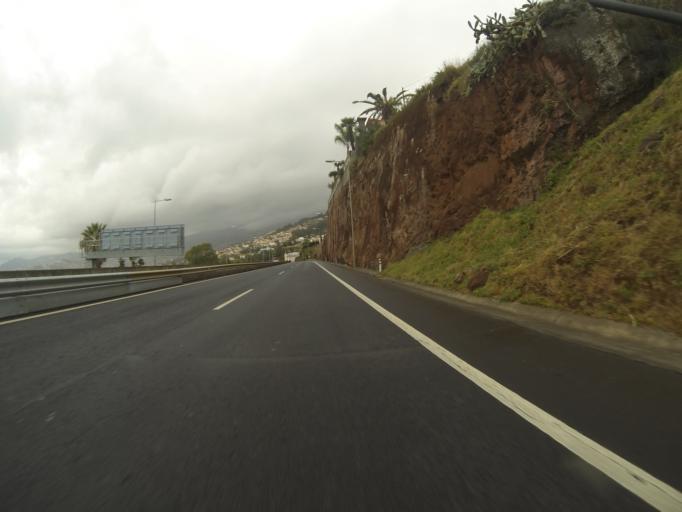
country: PT
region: Madeira
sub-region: Funchal
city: Nossa Senhora do Monte
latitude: 32.6519
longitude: -16.8764
